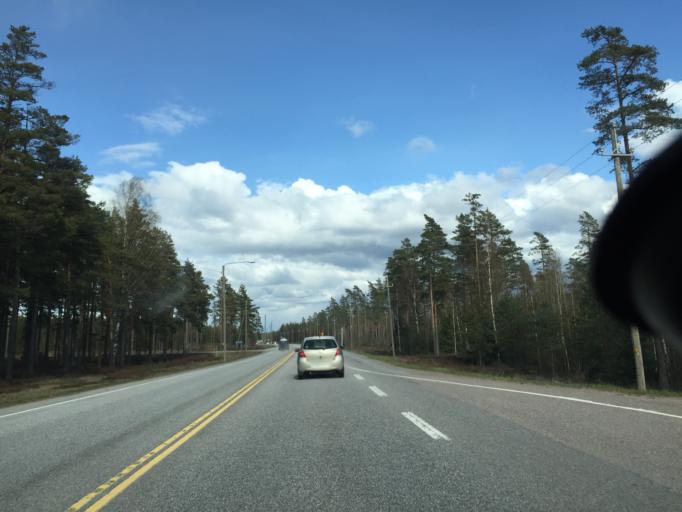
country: FI
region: Uusimaa
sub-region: Raaseporin
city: Pohja
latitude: 60.0084
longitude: 23.5433
